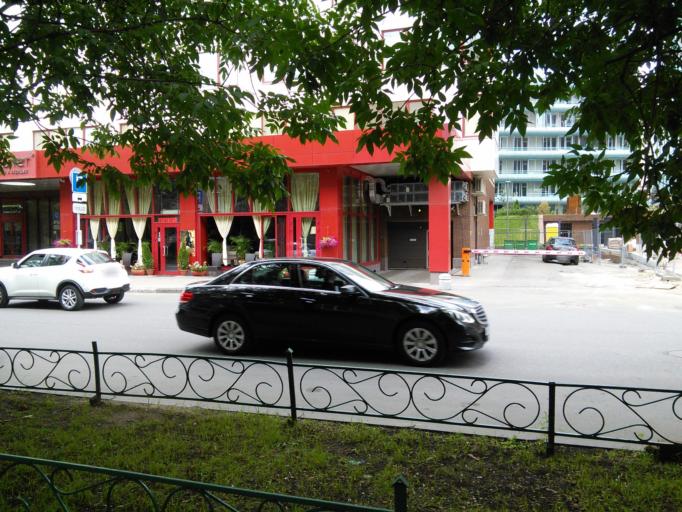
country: RU
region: Moscow
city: Luzhniki
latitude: 55.7250
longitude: 37.5747
